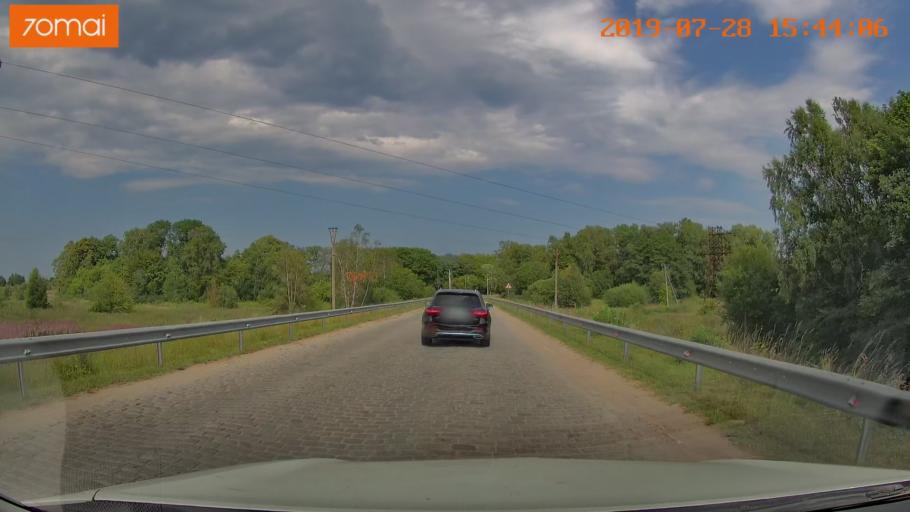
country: RU
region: Kaliningrad
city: Donskoye
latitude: 54.9391
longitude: 20.0287
